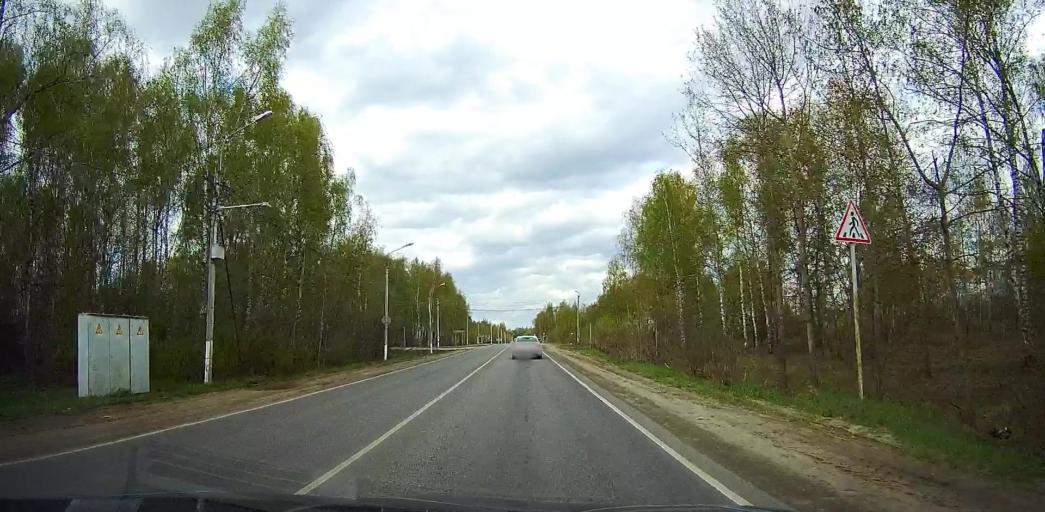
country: RU
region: Moskovskaya
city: Pavlovskiy Posad
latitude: 55.7573
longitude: 38.6559
